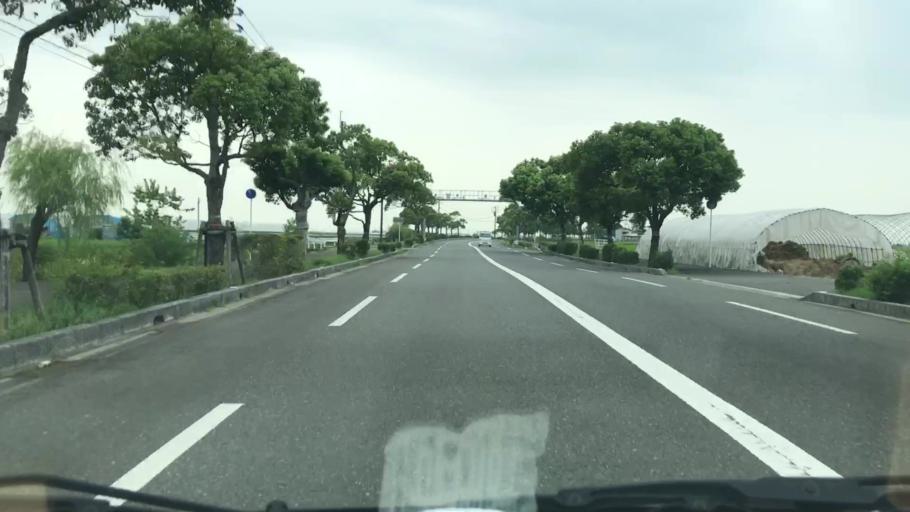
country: JP
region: Saga Prefecture
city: Okawa
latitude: 33.1943
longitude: 130.3036
